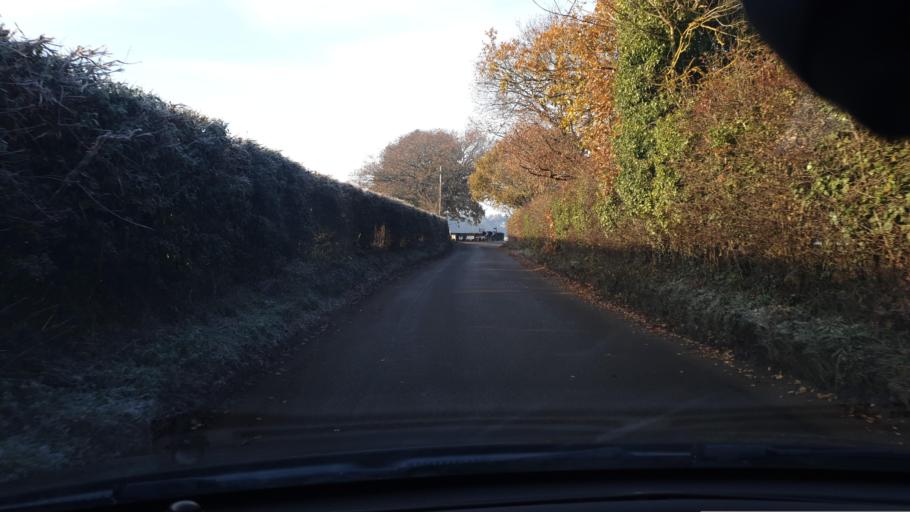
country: GB
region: England
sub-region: Essex
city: Mistley
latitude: 51.9771
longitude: 1.1158
